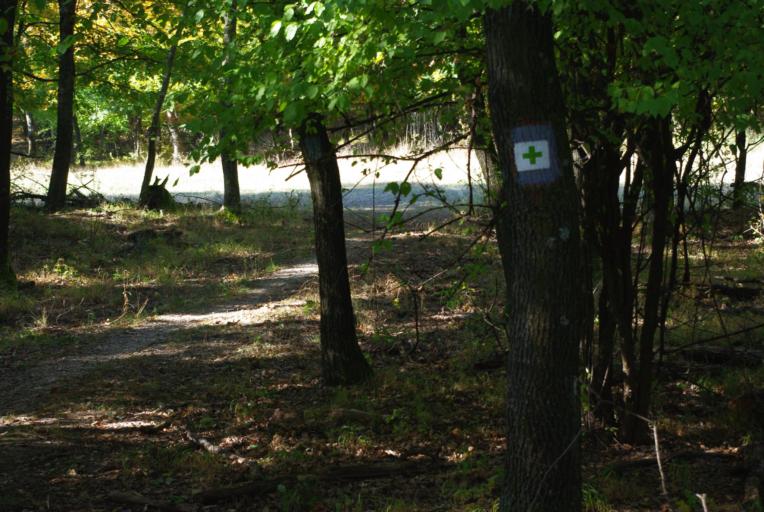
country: HU
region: Pest
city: Budakeszi
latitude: 47.5345
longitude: 18.9296
